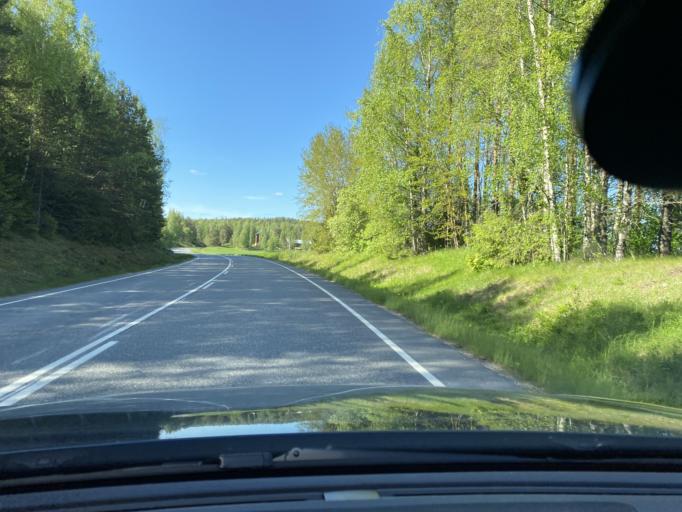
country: FI
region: Varsinais-Suomi
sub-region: Turku
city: Sauvo
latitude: 60.3749
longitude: 22.6702
